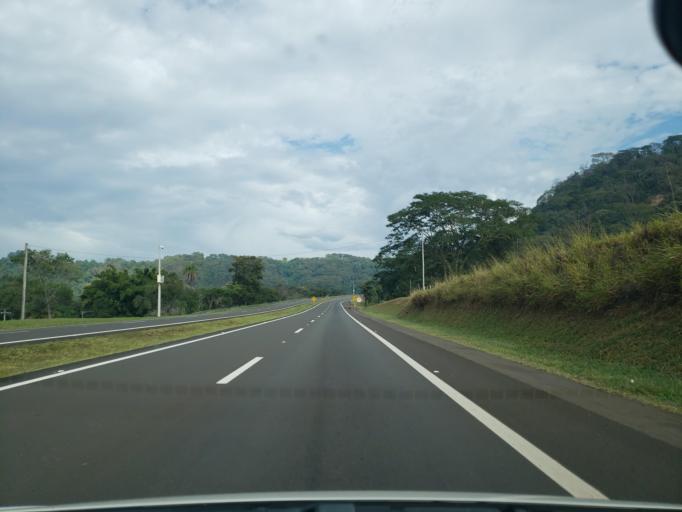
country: BR
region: Sao Paulo
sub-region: Dois Corregos
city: Dois Corregos
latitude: -22.2481
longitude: -48.3335
